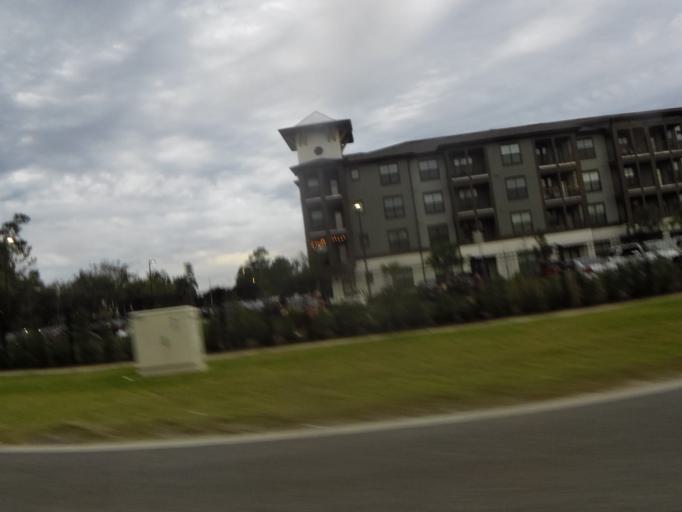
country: US
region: Florida
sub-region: Duval County
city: Jacksonville
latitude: 30.2466
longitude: -81.5881
